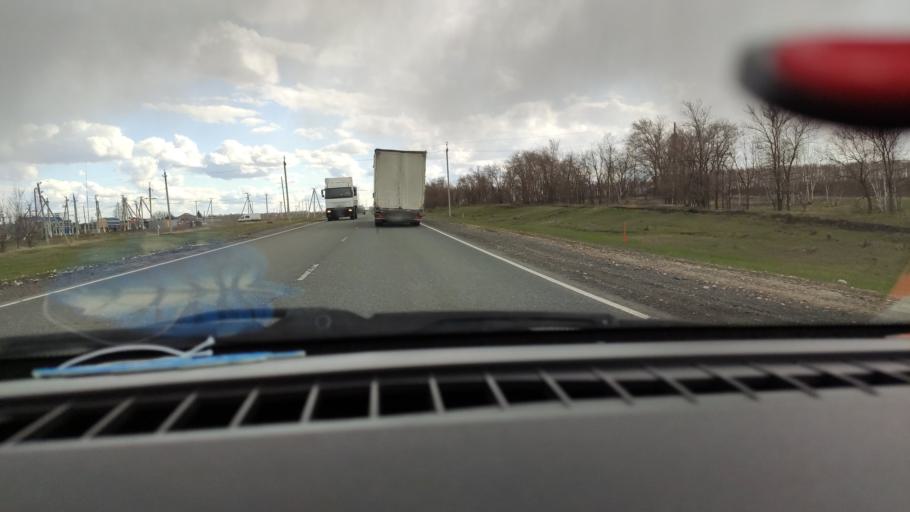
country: RU
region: Saratov
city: Balakovo
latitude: 52.1182
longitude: 47.7517
